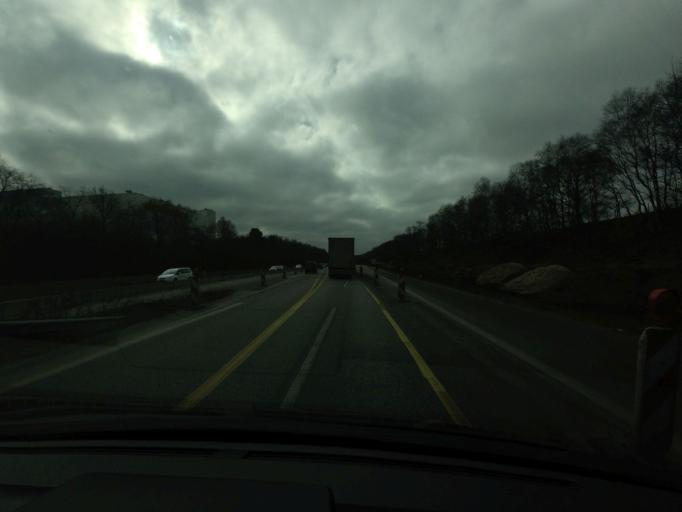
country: DE
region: Schleswig-Holstein
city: Nutzen
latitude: 53.8458
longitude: 9.9333
